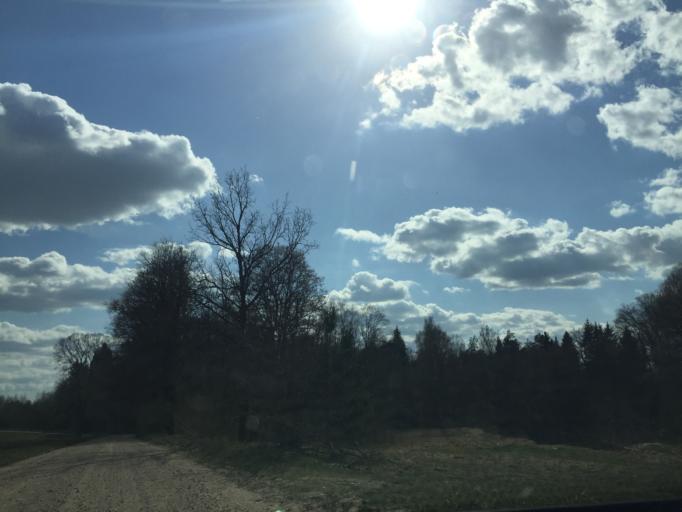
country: LV
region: Skriveri
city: Skriveri
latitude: 56.7807
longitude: 25.1957
